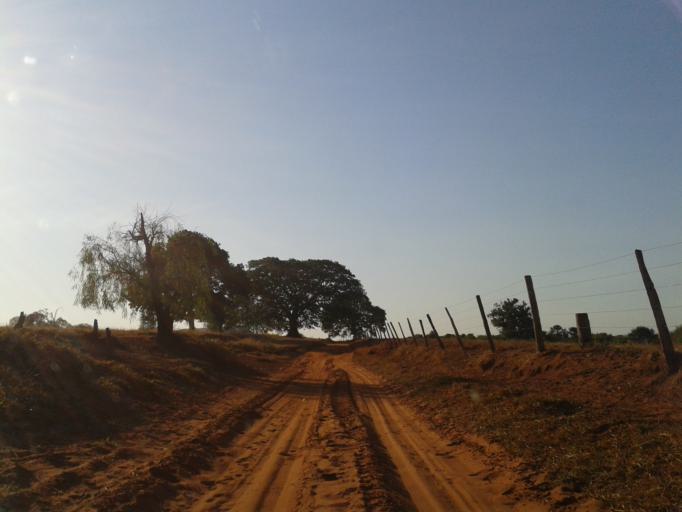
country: BR
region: Minas Gerais
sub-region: Santa Vitoria
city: Santa Vitoria
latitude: -19.1628
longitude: -50.0134
